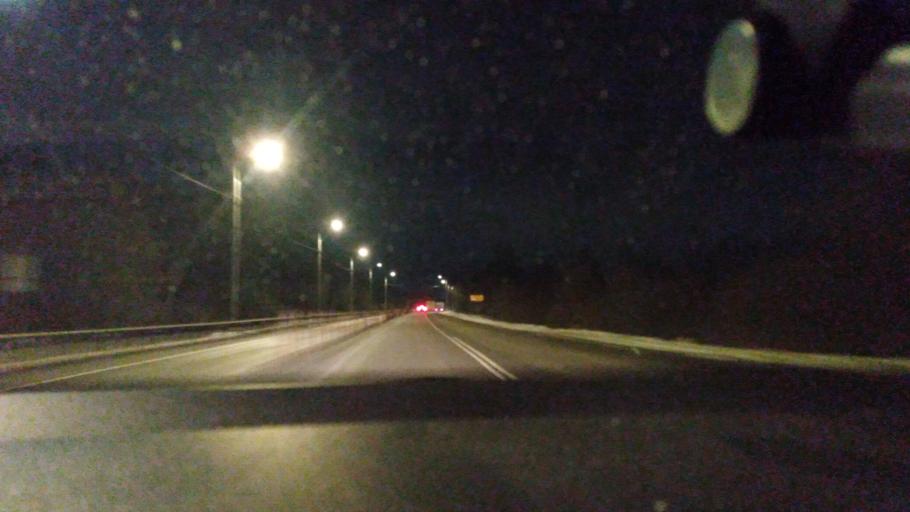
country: RU
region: Moskovskaya
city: Yegor'yevsk
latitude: 55.4480
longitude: 39.0098
